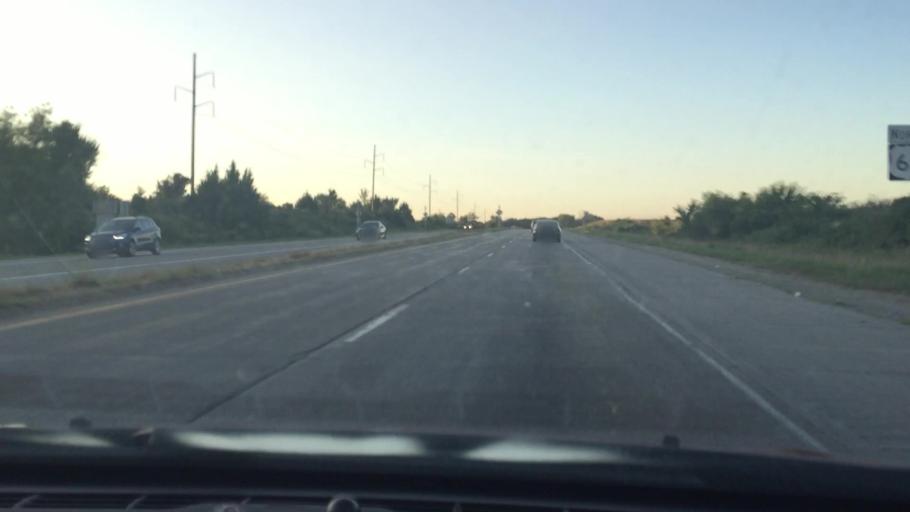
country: US
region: Iowa
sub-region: Muscatine County
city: Muscatine
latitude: 41.4366
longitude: -91.0919
